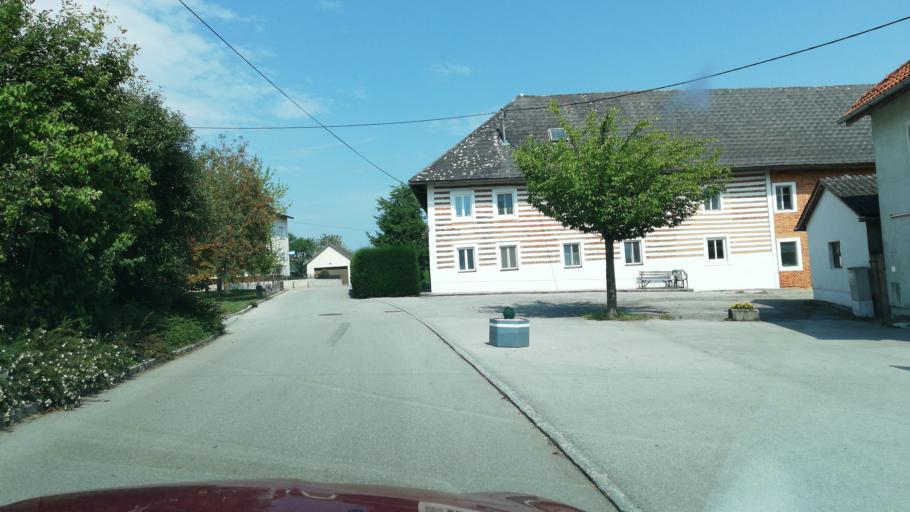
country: AT
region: Upper Austria
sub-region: Politischer Bezirk Steyr-Land
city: Sierning
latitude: 48.0505
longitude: 14.3066
